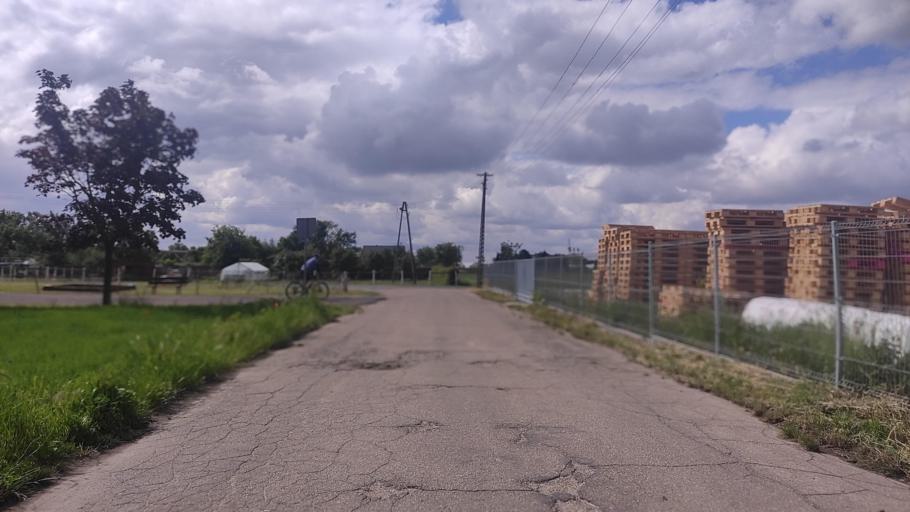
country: PL
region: Greater Poland Voivodeship
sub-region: Powiat poznanski
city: Kostrzyn
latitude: 52.4151
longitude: 17.1703
